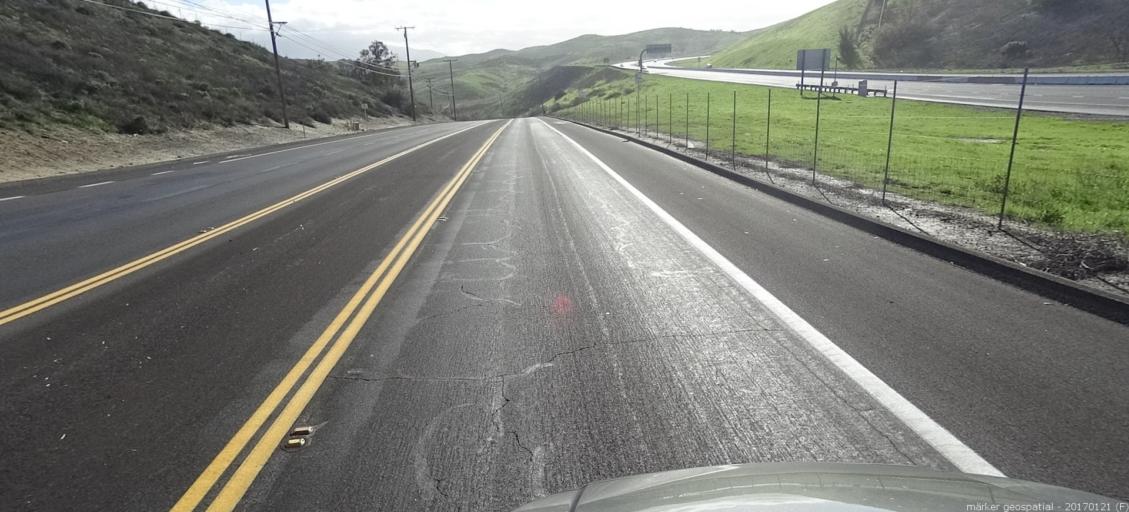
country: US
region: California
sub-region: Orange County
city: North Tustin
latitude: 33.7707
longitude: -117.7385
